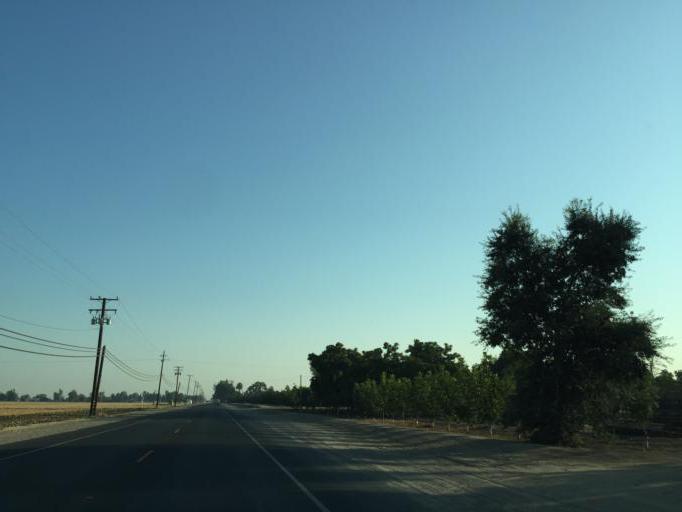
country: US
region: California
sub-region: Tulare County
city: Visalia
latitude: 36.3949
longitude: -119.2964
